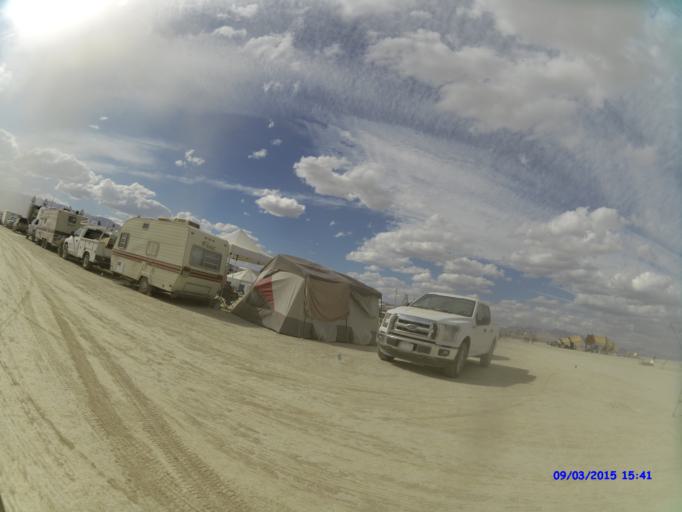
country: US
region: Nevada
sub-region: Pershing County
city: Lovelock
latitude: 40.7948
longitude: -119.2097
